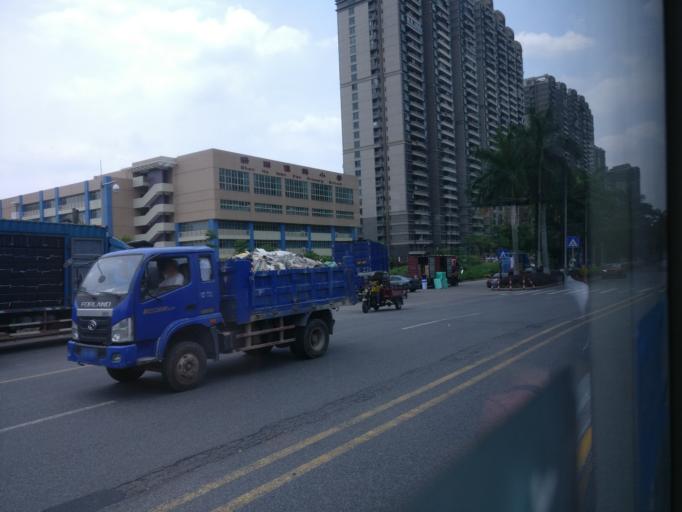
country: CN
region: Guangdong
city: Xiaoguwei
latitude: 23.0364
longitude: 113.3380
